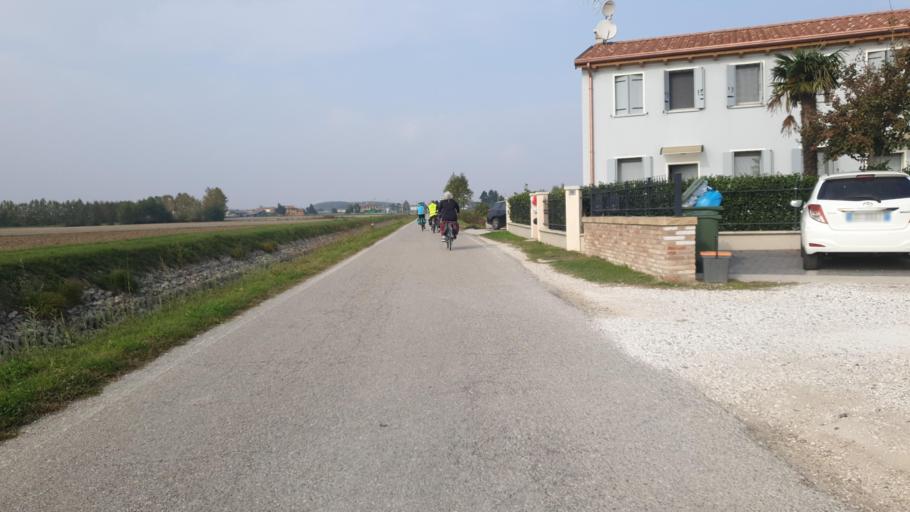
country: IT
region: Veneto
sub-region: Provincia di Padova
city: Vallonga
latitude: 45.2907
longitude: 12.0843
